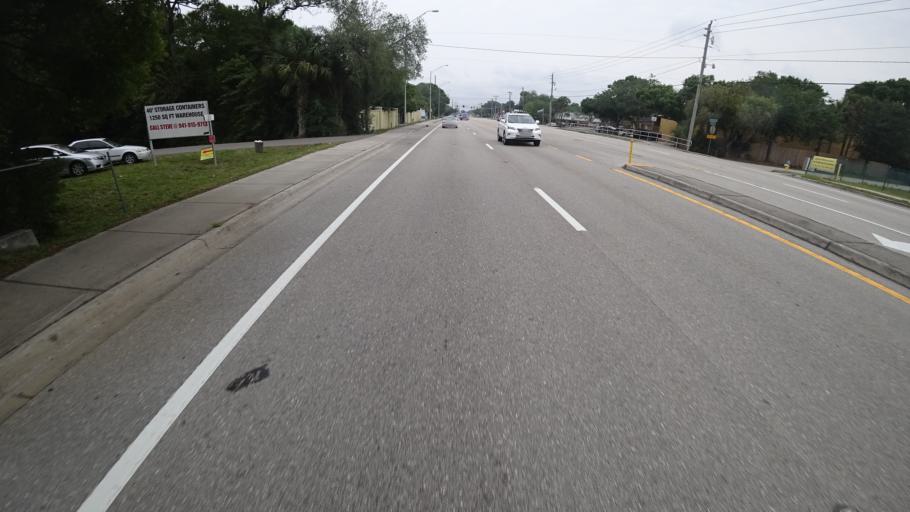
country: US
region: Florida
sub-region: Manatee County
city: Whitfield
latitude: 27.4294
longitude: -82.5489
